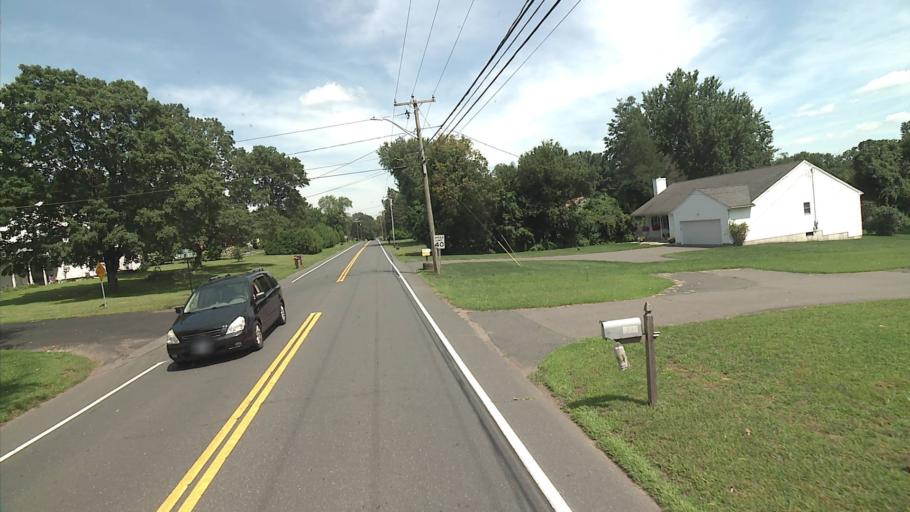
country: US
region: Connecticut
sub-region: Tolland County
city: Ellington
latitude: 41.8937
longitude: -72.4802
